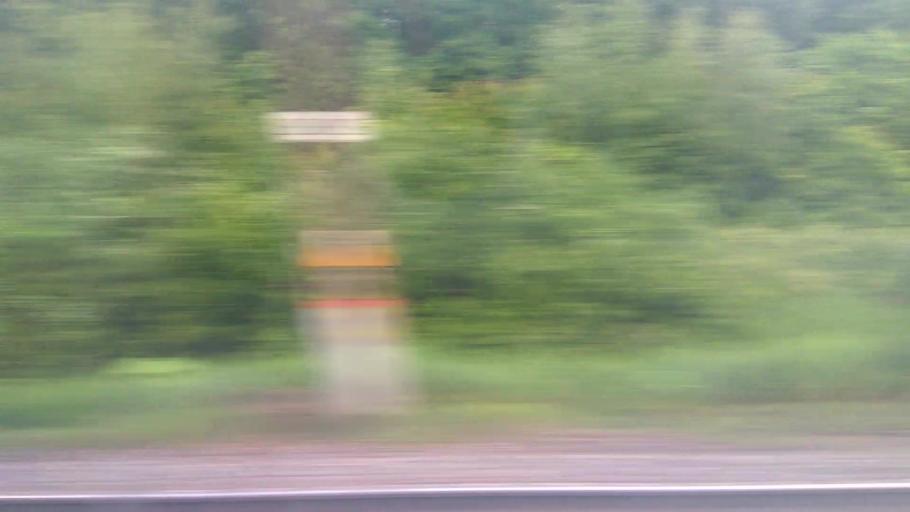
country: RU
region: Moskovskaya
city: Mikhnevo
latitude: 55.0909
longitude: 37.9684
